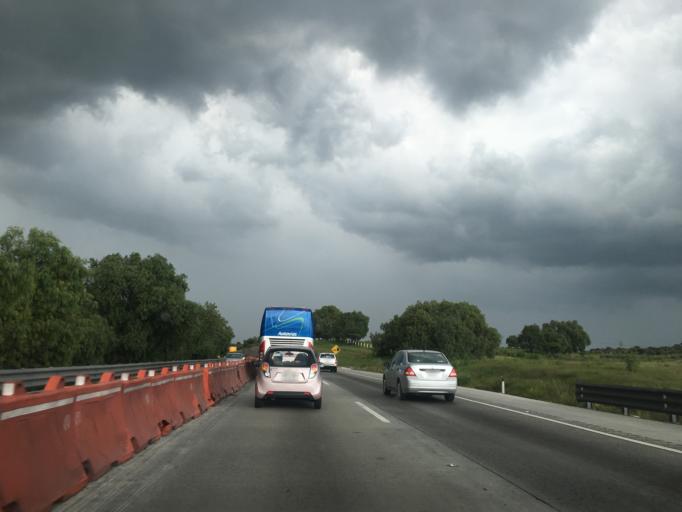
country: MX
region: Hidalgo
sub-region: Tepeji del Rio de Ocampo
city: Santiago Tlapanaloya
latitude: 19.8646
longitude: -99.3313
